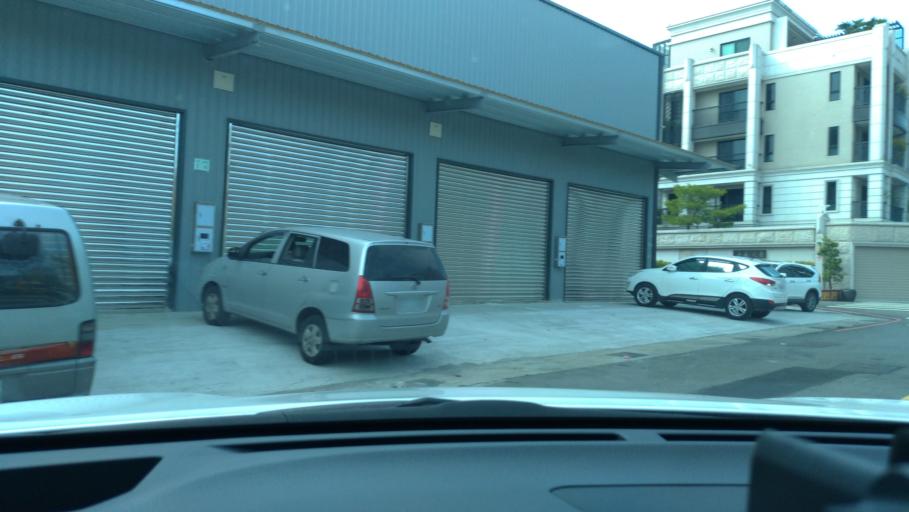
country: TW
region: Taiwan
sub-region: Taichung City
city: Taichung
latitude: 24.1672
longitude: 120.7302
